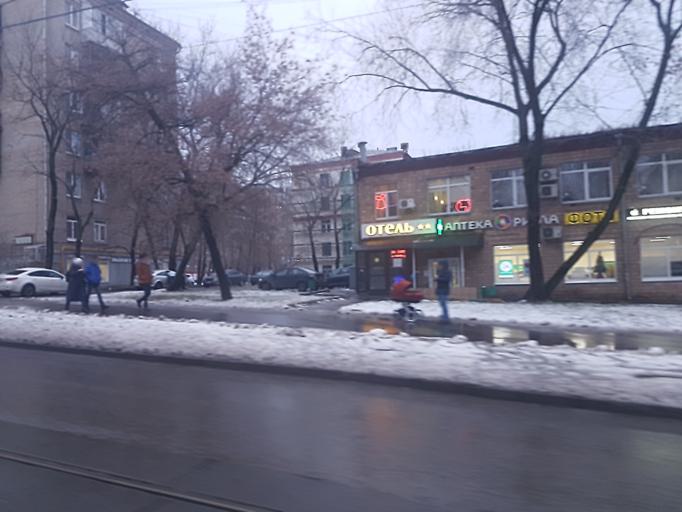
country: RU
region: Moskovskaya
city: Kozhukhovo
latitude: 55.6776
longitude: 37.6587
